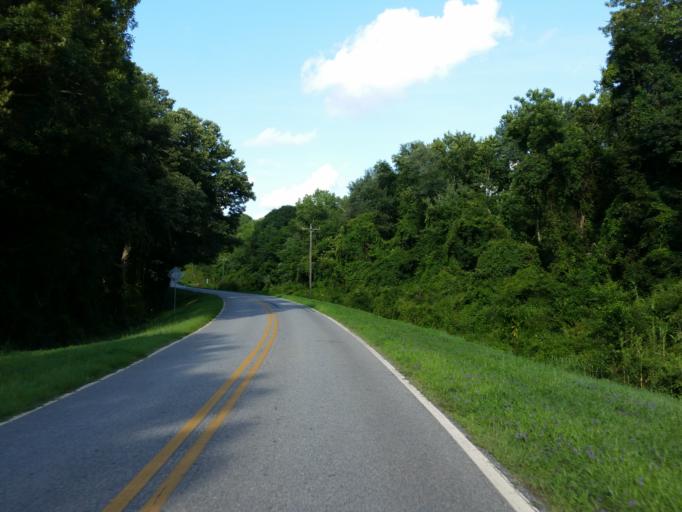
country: US
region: Georgia
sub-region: Lee County
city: Leesburg
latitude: 31.9113
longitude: -84.0250
